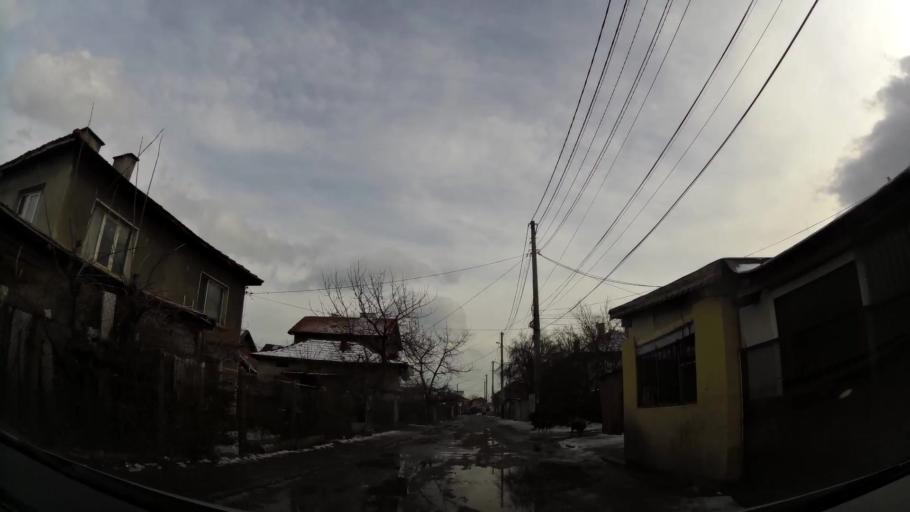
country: BG
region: Sofia-Capital
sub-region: Stolichna Obshtina
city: Sofia
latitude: 42.6880
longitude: 23.3847
